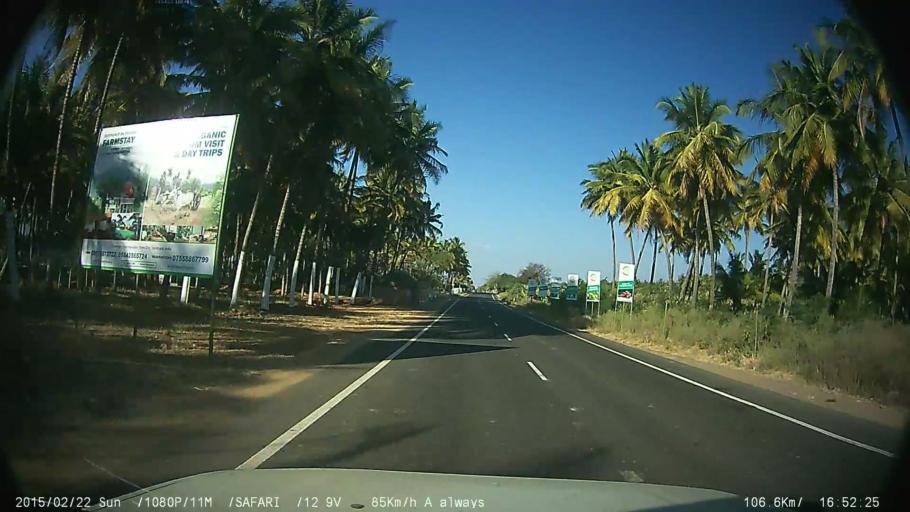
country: IN
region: Tamil Nadu
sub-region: Theni
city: Gudalur
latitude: 9.6579
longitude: 77.2248
